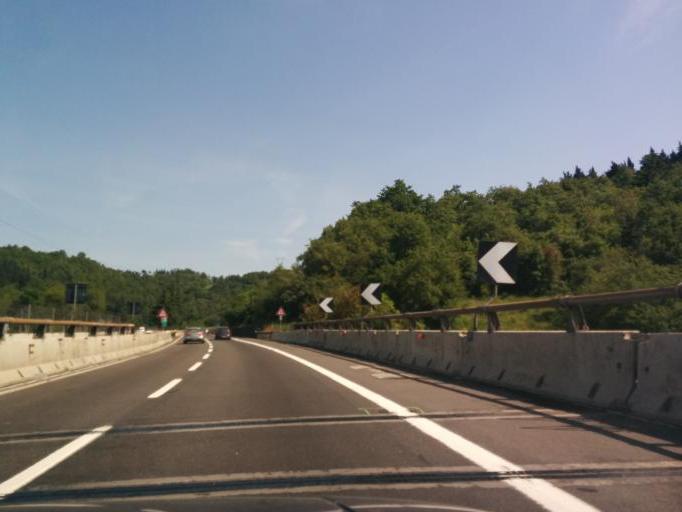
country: IT
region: Tuscany
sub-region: Province of Florence
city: Cavallina
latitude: 43.9363
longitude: 11.2221
